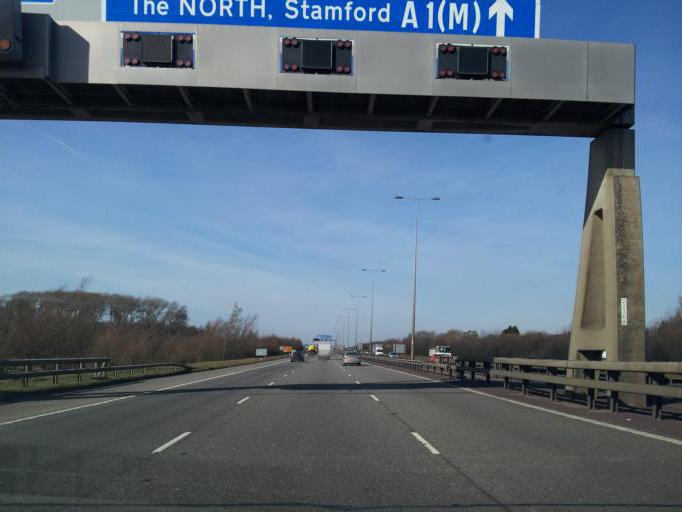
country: GB
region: England
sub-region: Cambridgeshire
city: Stilton
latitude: 52.5180
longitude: -0.3020
